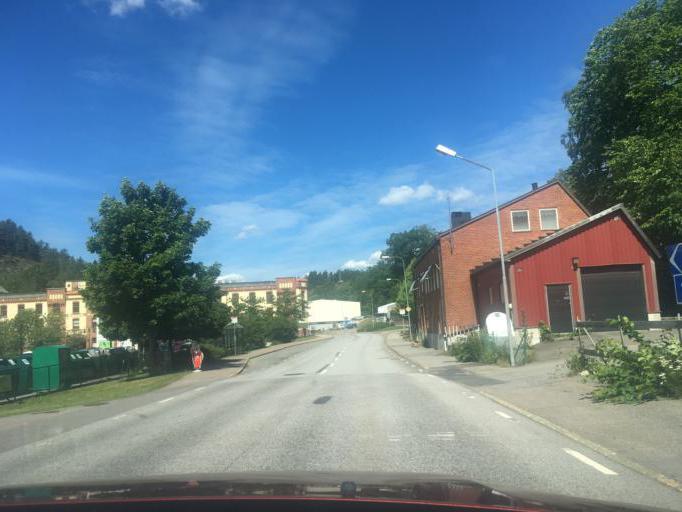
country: SE
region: OEstergoetland
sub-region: Valdemarsviks Kommun
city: Valdemarsvik
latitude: 58.2041
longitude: 16.6047
